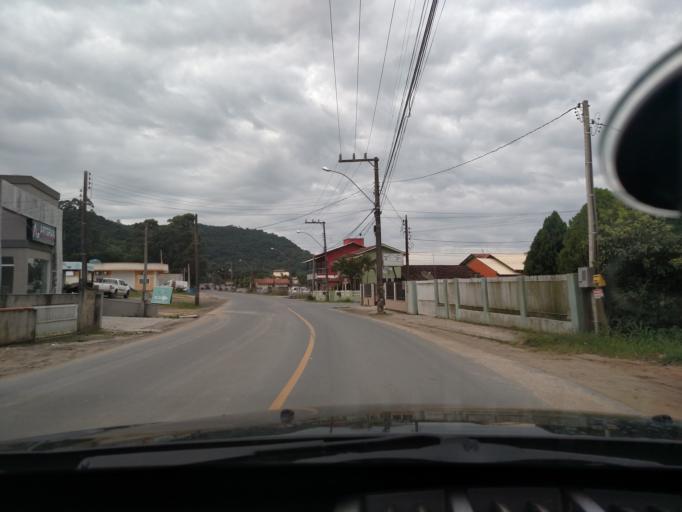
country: BR
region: Santa Catarina
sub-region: Porto Belo
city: Porto Belo
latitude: -27.1633
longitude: -48.5196
